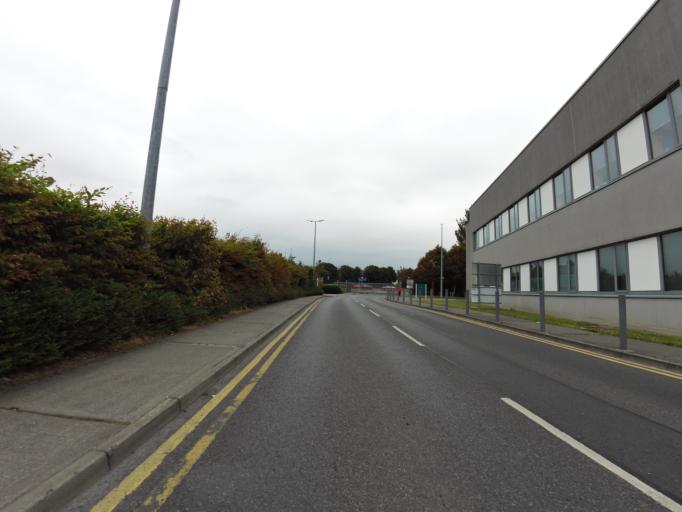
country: IE
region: Connaught
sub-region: County Galway
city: Gaillimh
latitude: 53.2782
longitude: -9.0685
